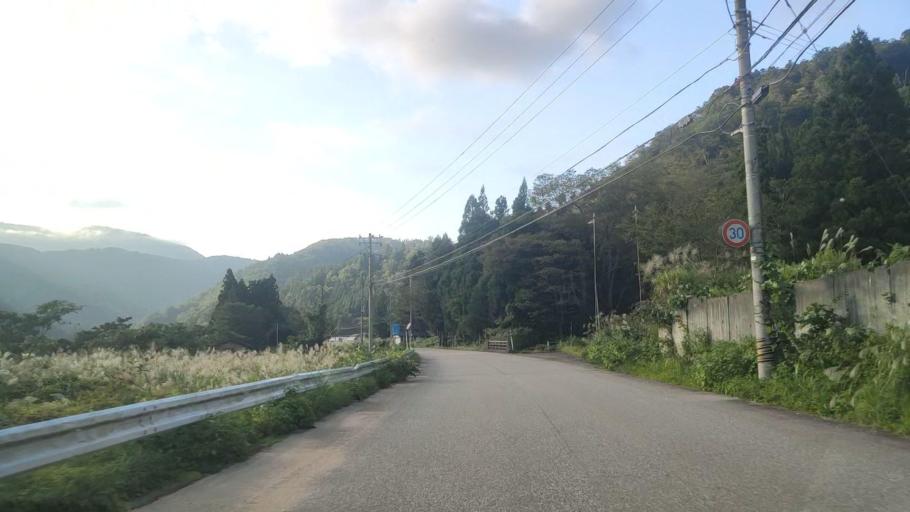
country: JP
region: Toyama
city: Yatsuomachi-higashikumisaka
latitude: 36.4777
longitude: 137.0839
